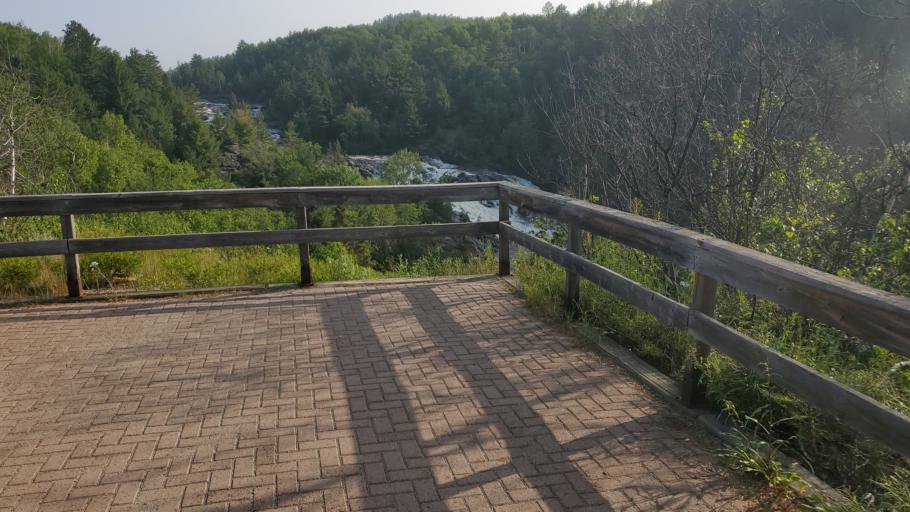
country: CA
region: Ontario
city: Rayside-Balfour
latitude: 46.5894
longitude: -81.3818
